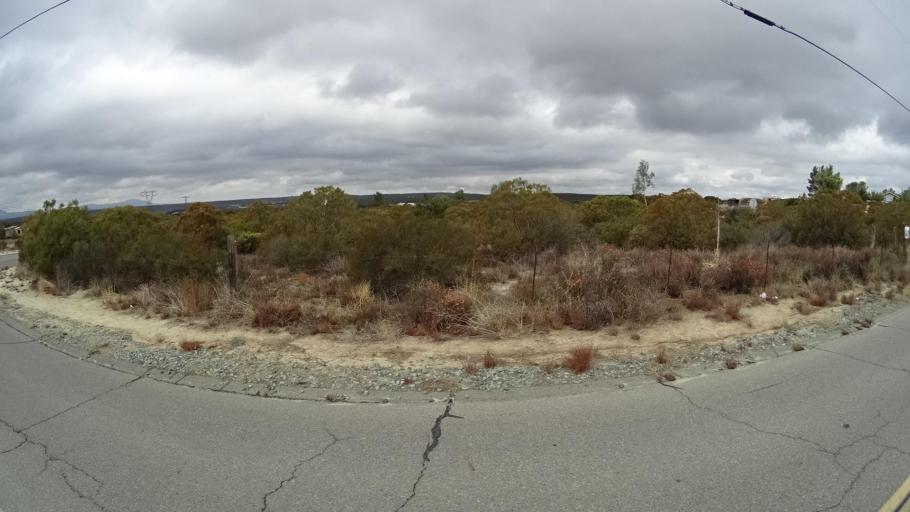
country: US
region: California
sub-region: San Diego County
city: Campo
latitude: 32.6060
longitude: -116.3339
